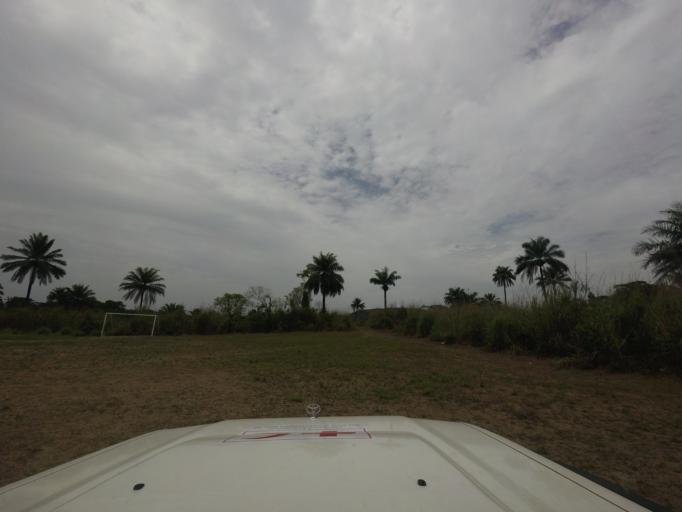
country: SL
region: Eastern Province
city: Buedu
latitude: 8.4253
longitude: -10.2628
